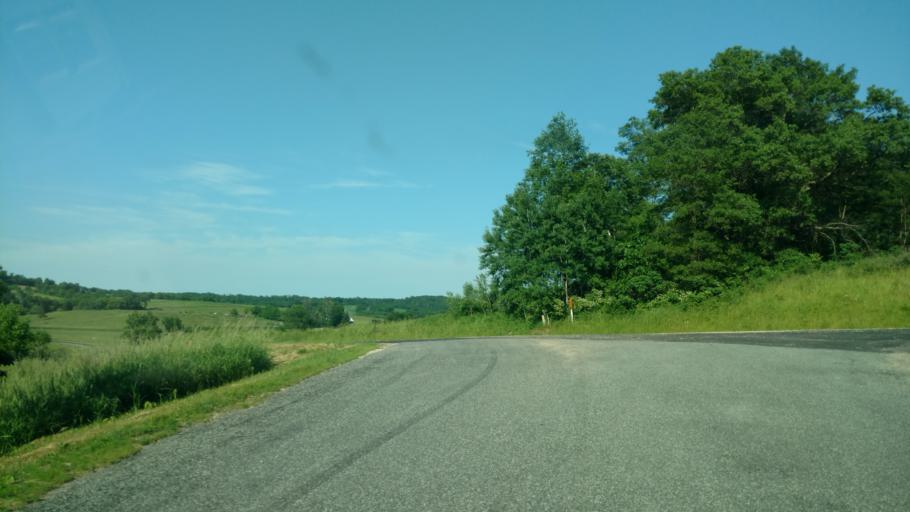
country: US
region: Wisconsin
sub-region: Vernon County
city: Hillsboro
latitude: 43.6856
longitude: -90.3455
